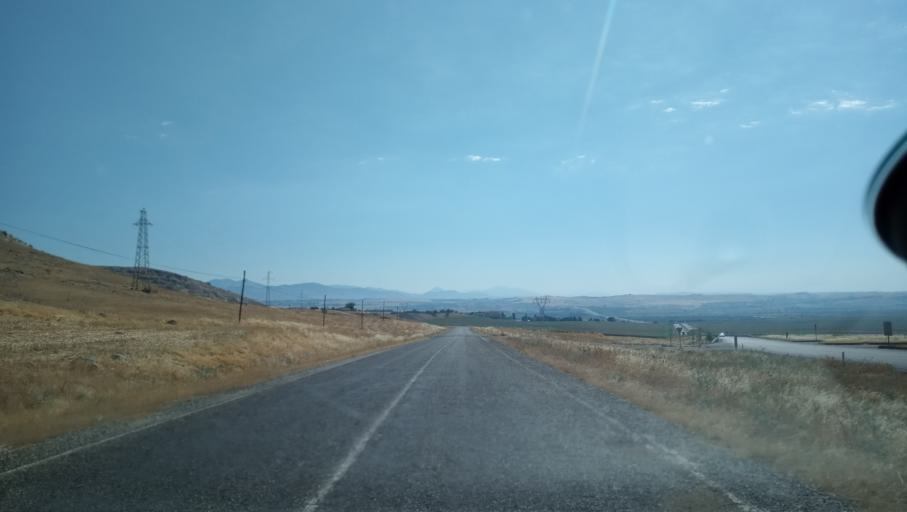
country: TR
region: Diyarbakir
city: Malabadi
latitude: 38.1284
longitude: 41.1742
